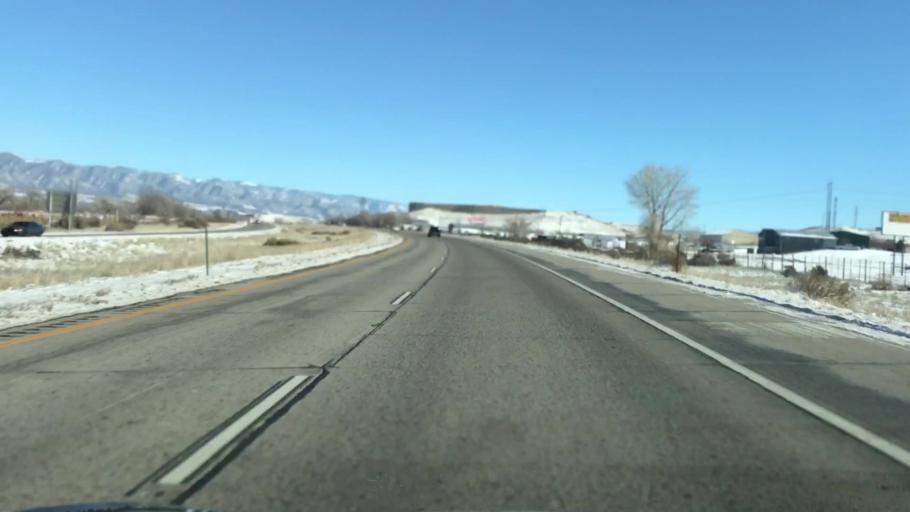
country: US
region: Colorado
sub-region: Garfield County
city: Rifle
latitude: 39.5250
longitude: -107.7532
